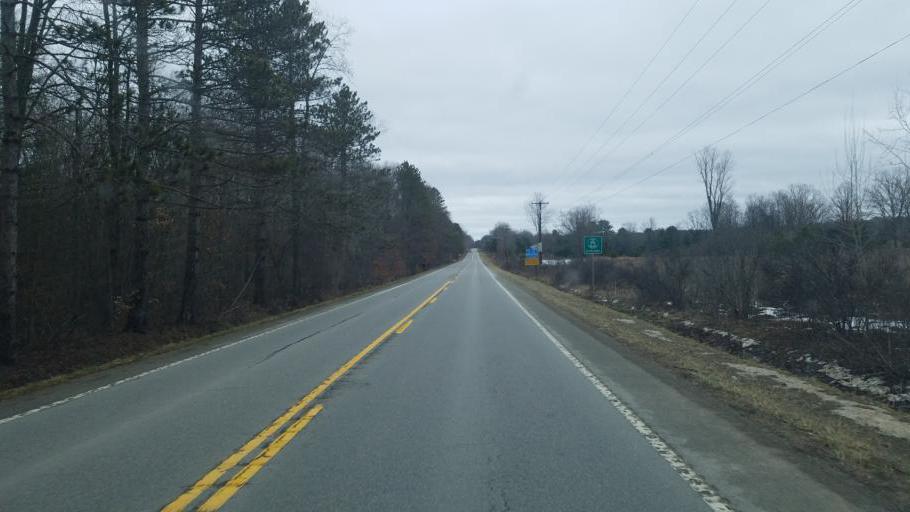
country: US
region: Pennsylvania
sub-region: Forest County
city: Marienville
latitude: 41.4226
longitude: -79.2058
